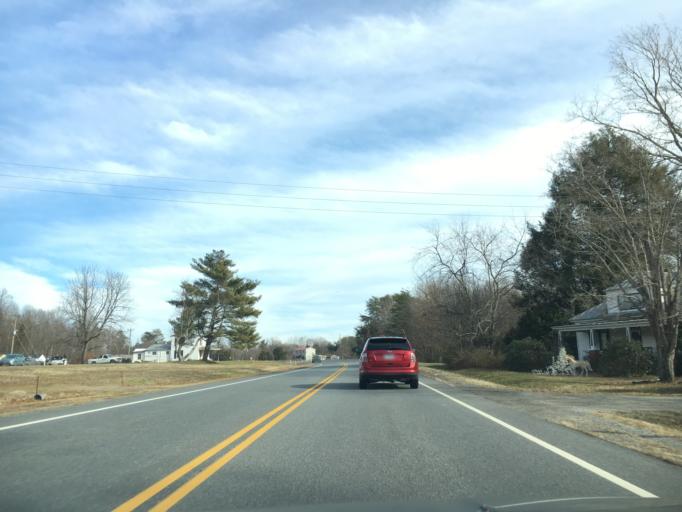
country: US
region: Virginia
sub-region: Louisa County
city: Louisa
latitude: 38.0442
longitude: -77.8835
